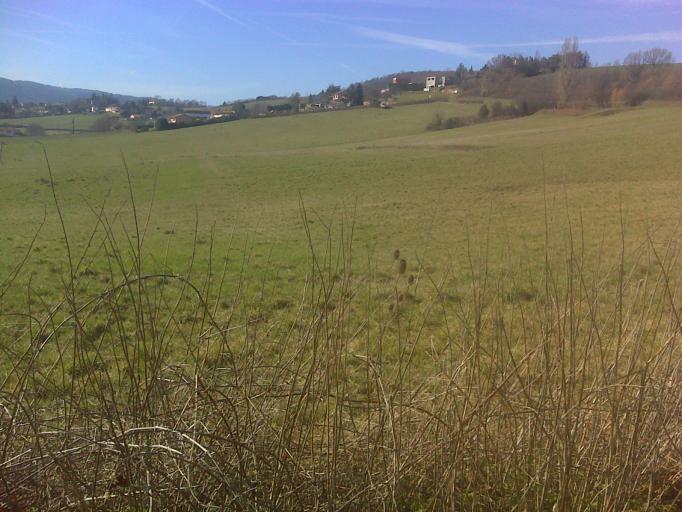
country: FR
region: Rhone-Alpes
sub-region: Departement du Rhone
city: Lentilly
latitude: 45.8190
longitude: 4.6465
